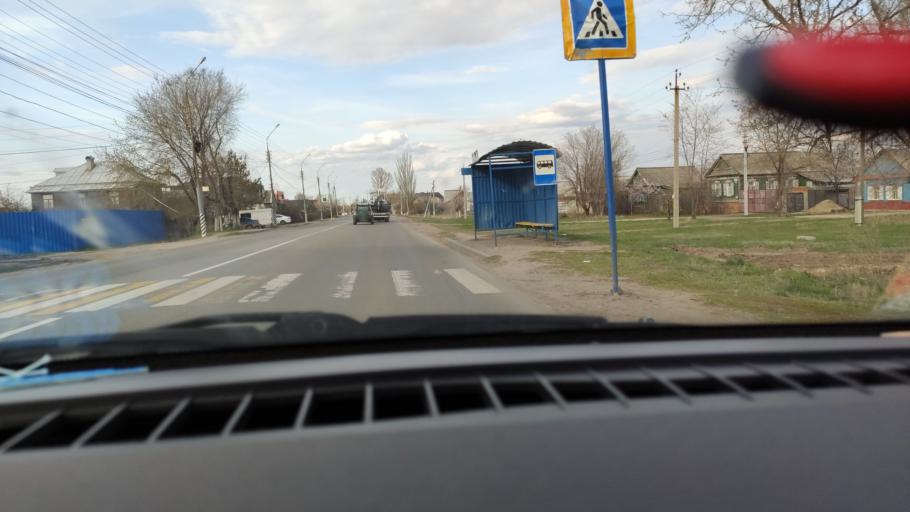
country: RU
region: Saratov
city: Privolzhskiy
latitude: 51.4307
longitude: 46.0545
